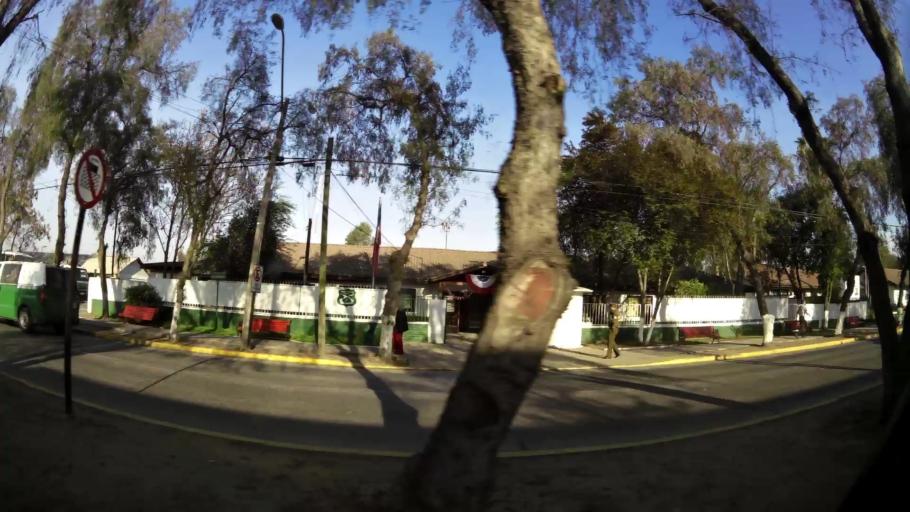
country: CL
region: Santiago Metropolitan
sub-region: Provincia de Santiago
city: Lo Prado
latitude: -33.4483
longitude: -70.7394
